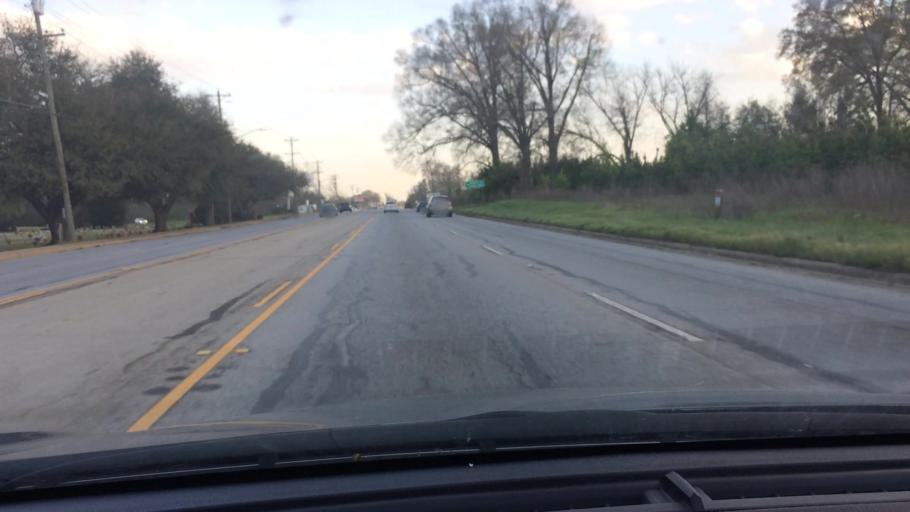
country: US
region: South Carolina
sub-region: Newberry County
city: Newberry
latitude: 34.2638
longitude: -81.5841
